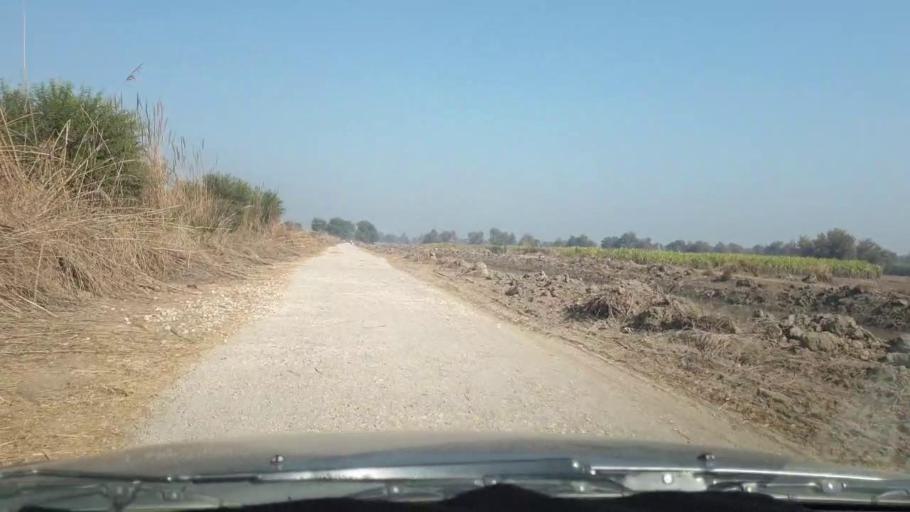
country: PK
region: Sindh
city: Khanpur
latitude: 27.7703
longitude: 69.5336
